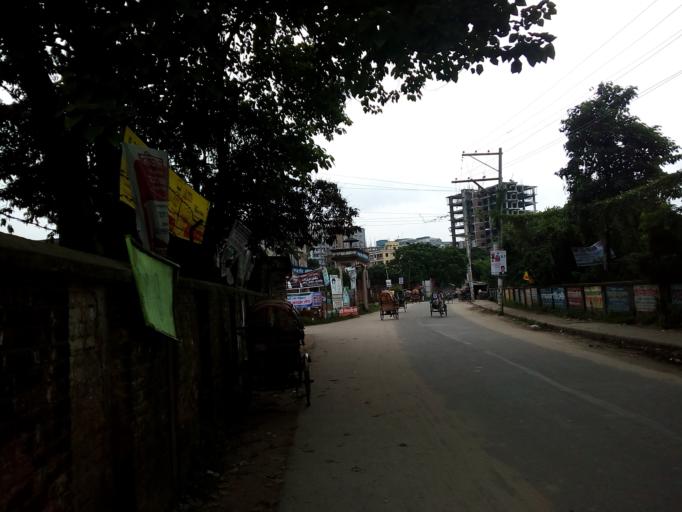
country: BD
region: Dhaka
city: Tungi
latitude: 23.8391
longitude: 90.2496
